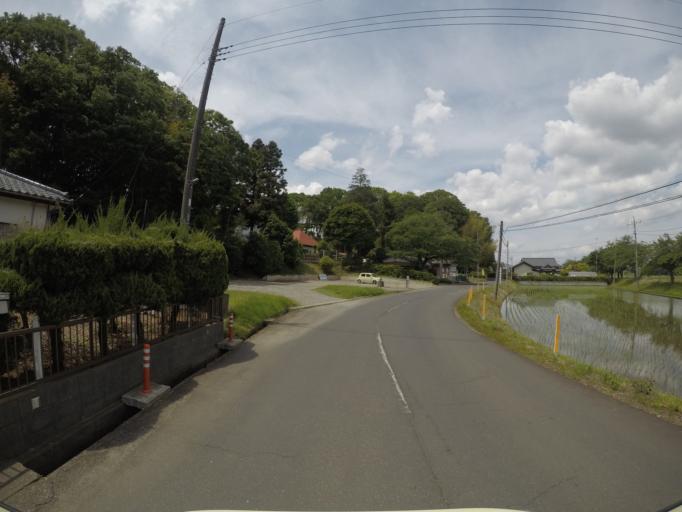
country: JP
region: Ibaraki
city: Ushiku
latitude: 35.9614
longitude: 140.1222
